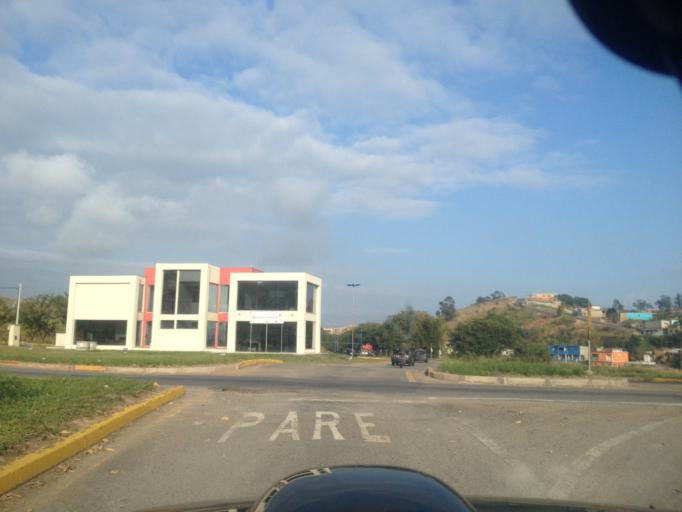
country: BR
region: Rio de Janeiro
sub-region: Porto Real
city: Porto Real
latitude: -22.4454
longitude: -44.3163
